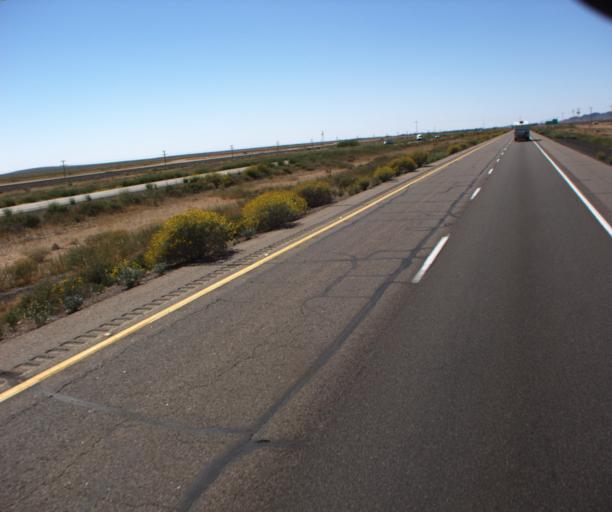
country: US
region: Arizona
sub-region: Maricopa County
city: Gila Bend
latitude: 32.9150
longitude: -112.9342
